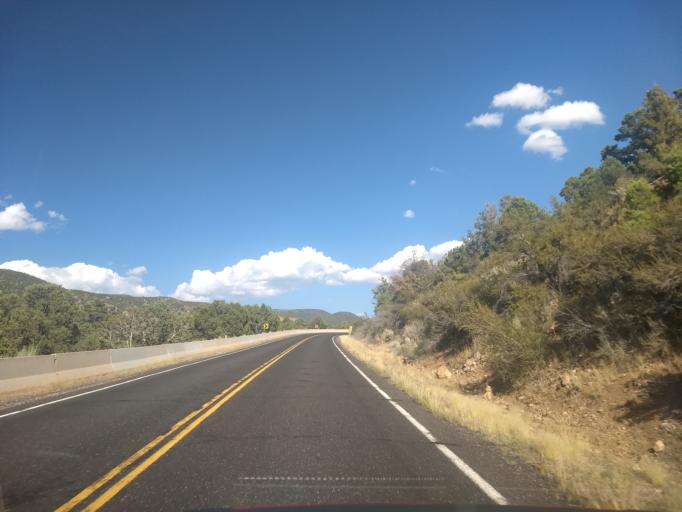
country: US
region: Utah
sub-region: Washington County
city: Enterprise
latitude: 37.4239
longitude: -113.5839
